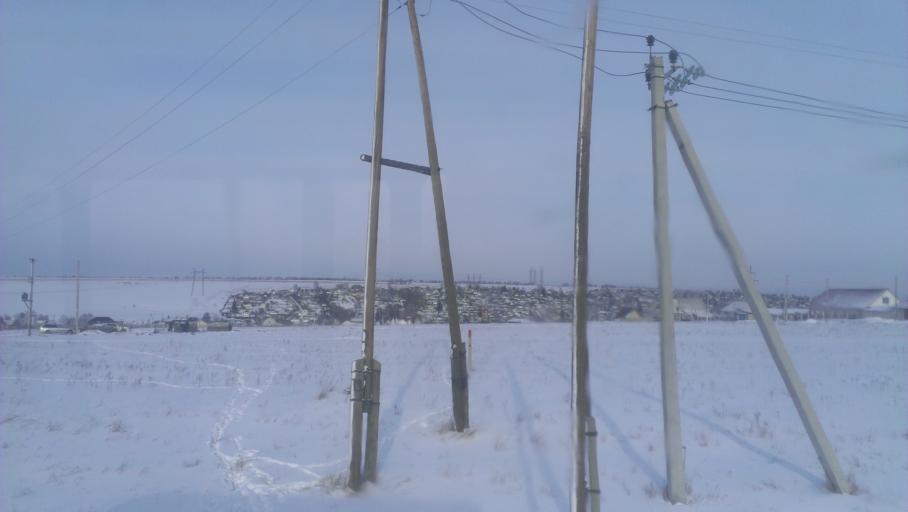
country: RU
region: Altai Krai
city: Gon'ba
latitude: 53.4121
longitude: 83.5589
